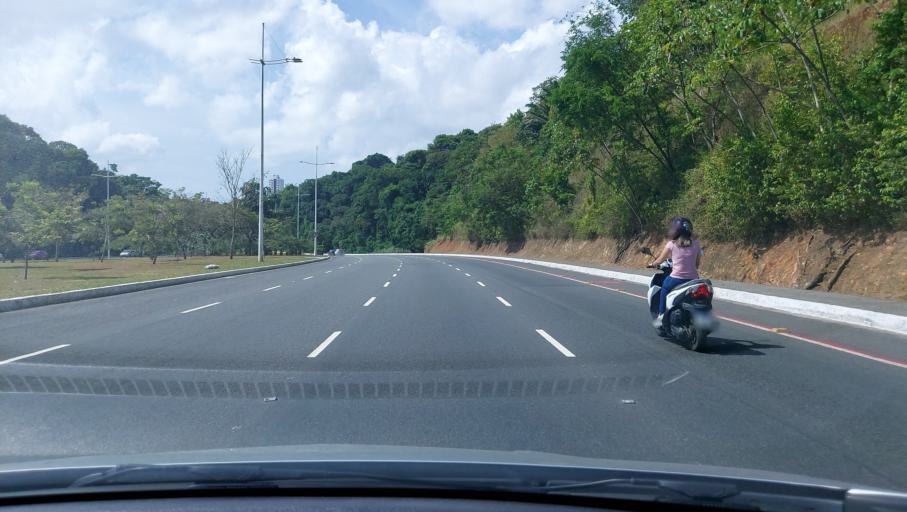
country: BR
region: Bahia
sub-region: Salvador
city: Salvador
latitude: -12.9637
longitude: -38.4583
